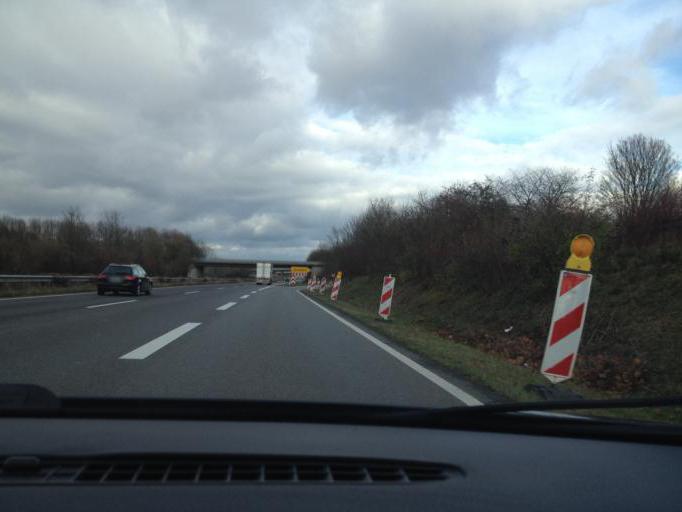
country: DE
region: Rheinland-Pfalz
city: Schwegenheim
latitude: 49.2649
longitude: 8.3354
